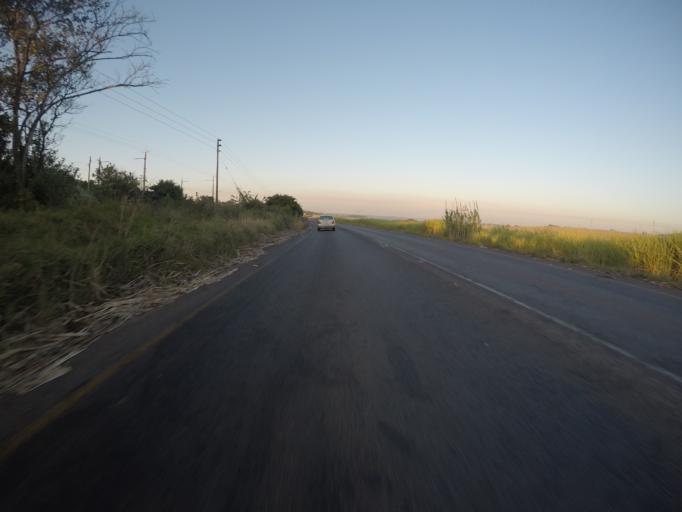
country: ZA
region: KwaZulu-Natal
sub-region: uThungulu District Municipality
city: Empangeni
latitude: -28.8062
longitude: 31.8923
